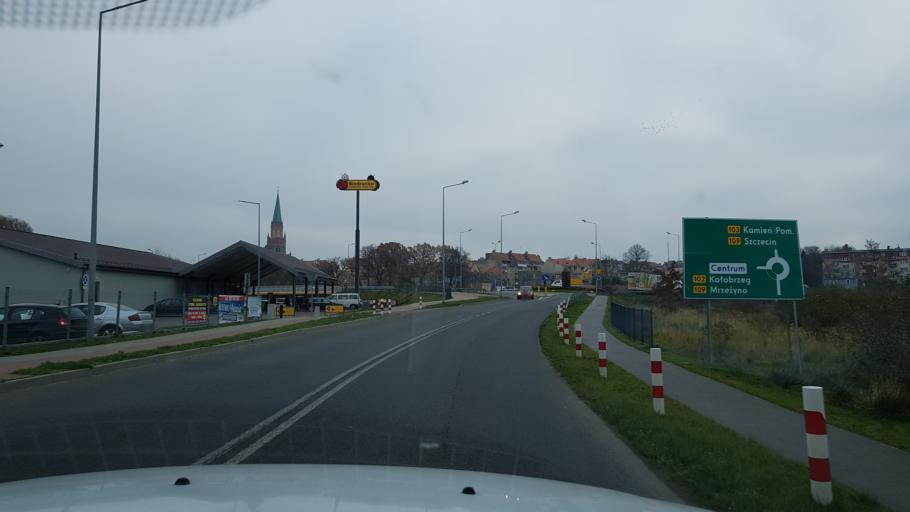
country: PL
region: West Pomeranian Voivodeship
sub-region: Powiat gryficki
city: Trzebiatow
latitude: 54.0637
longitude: 15.2577
